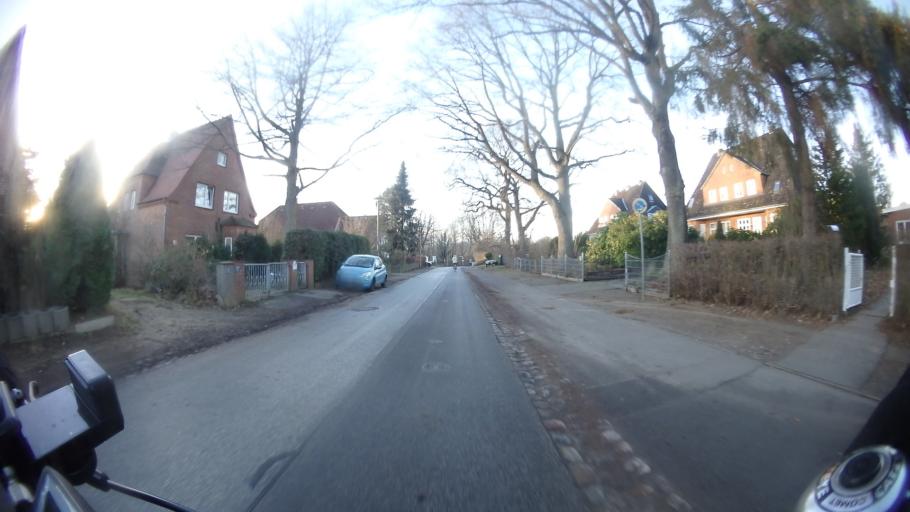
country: DE
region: Schleswig-Holstein
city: Ratekau
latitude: 53.9084
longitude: 10.7724
